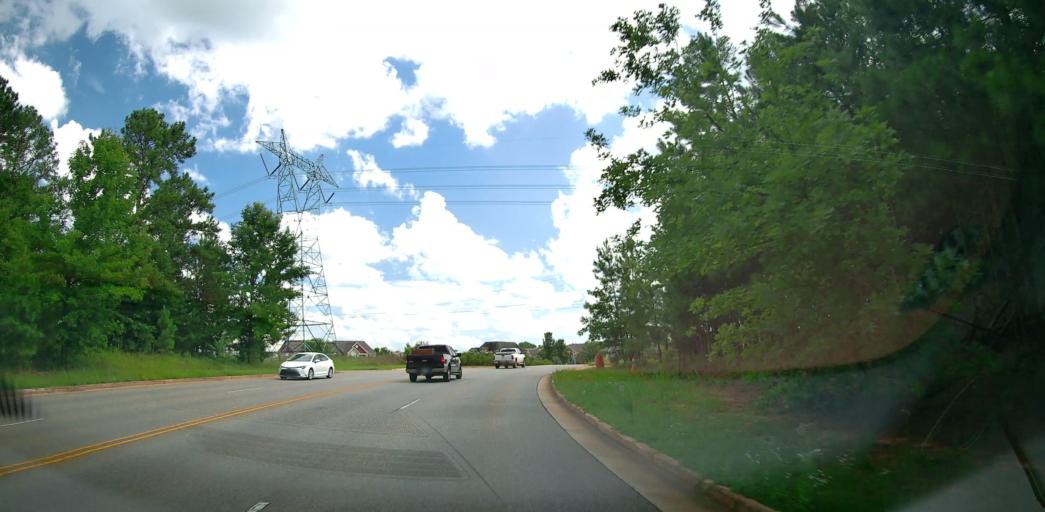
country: US
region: Georgia
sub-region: Houston County
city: Centerville
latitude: 32.5890
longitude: -83.6556
